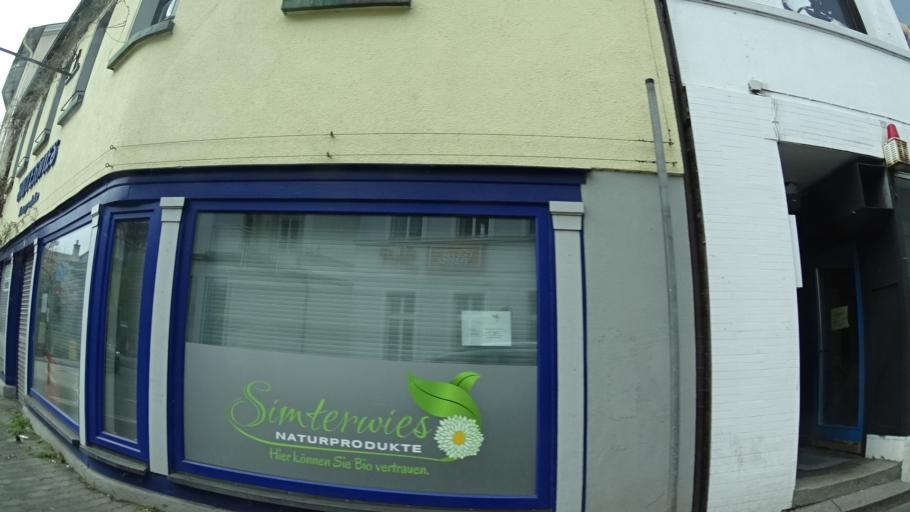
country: DE
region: Rheinland-Pfalz
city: Idar-Oberstein
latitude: 49.7224
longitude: 7.2985
